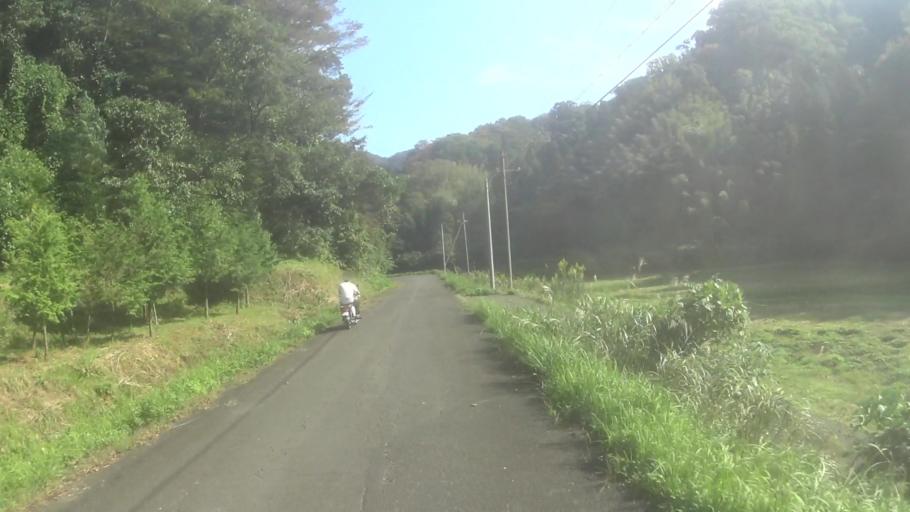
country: JP
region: Kyoto
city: Miyazu
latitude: 35.7150
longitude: 135.1262
